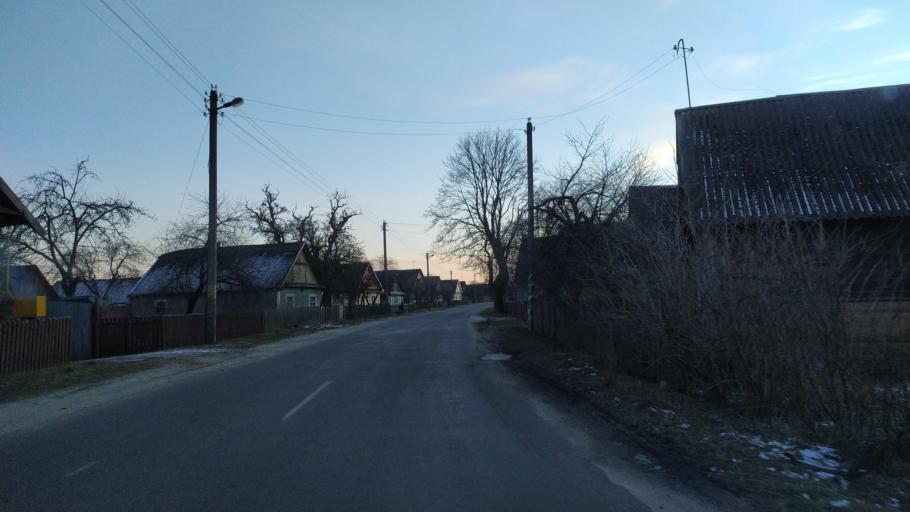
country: BY
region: Brest
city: Pruzhany
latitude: 52.5494
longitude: 24.2105
